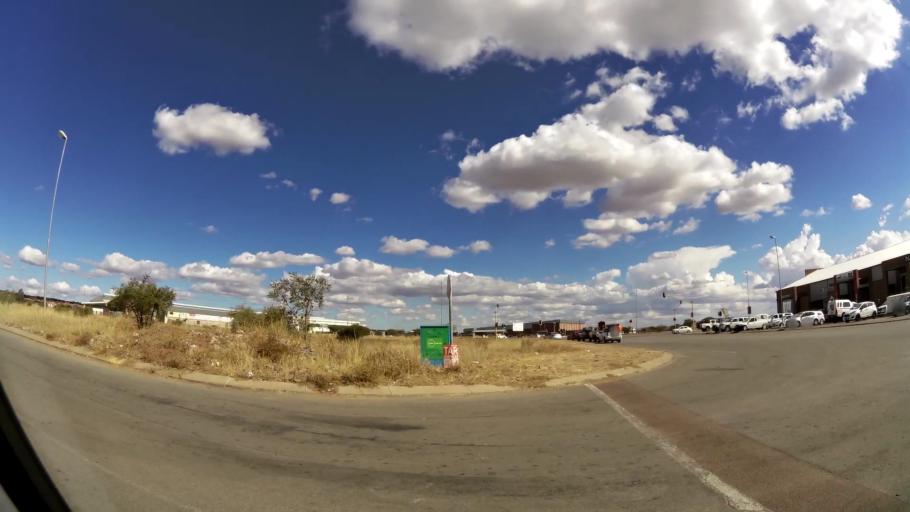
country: ZA
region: Limpopo
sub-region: Capricorn District Municipality
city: Polokwane
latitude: -23.8676
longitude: 29.4809
